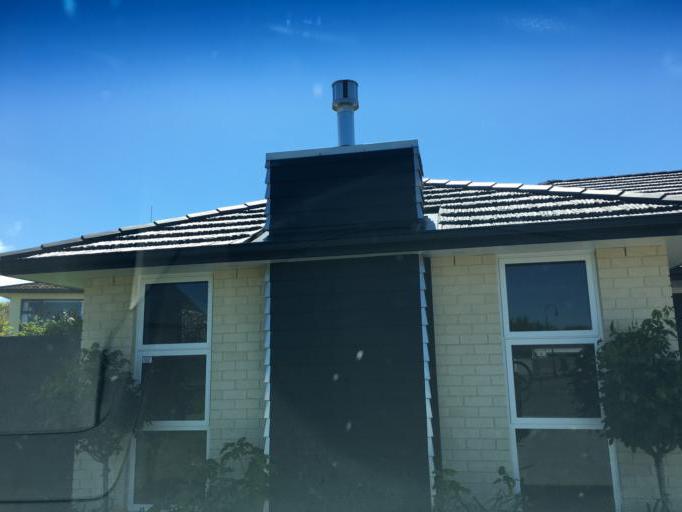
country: NZ
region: Manawatu-Wanganui
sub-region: Palmerston North City
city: Palmerston North
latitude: -40.3785
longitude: 175.5756
